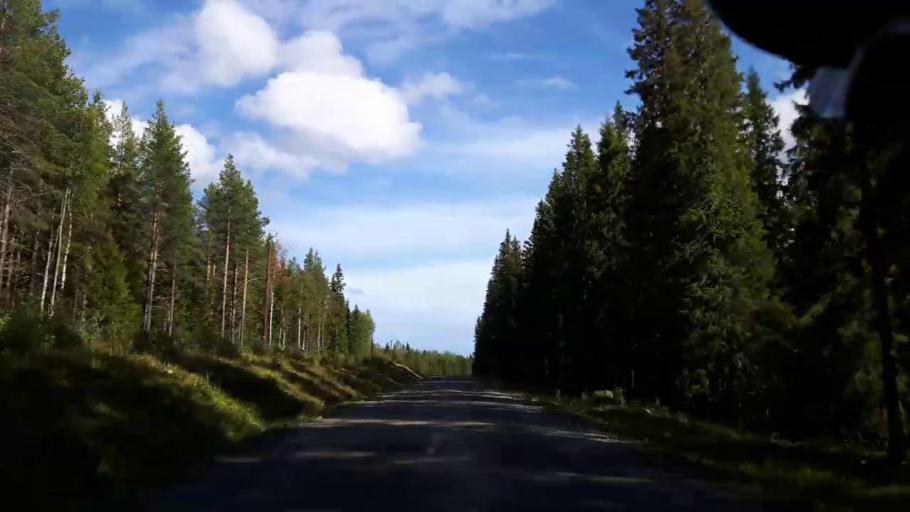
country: SE
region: Jaemtland
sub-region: Ragunda Kommun
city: Hammarstrand
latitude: 63.4341
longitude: 16.0336
